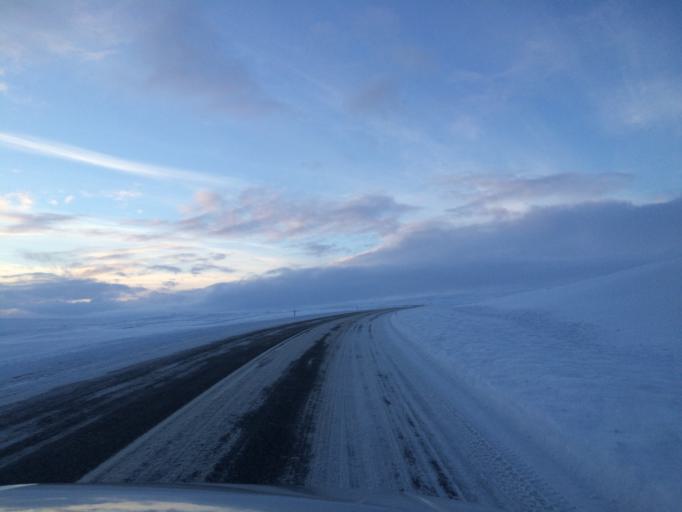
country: IS
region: South
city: Hveragerdi
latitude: 64.2239
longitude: -21.2161
